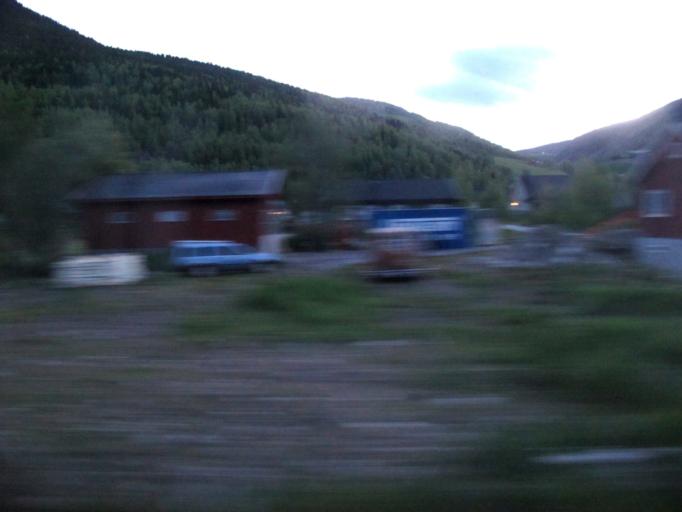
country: NO
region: Oppland
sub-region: Nord-Fron
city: Vinstra
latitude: 61.6629
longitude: 9.6748
